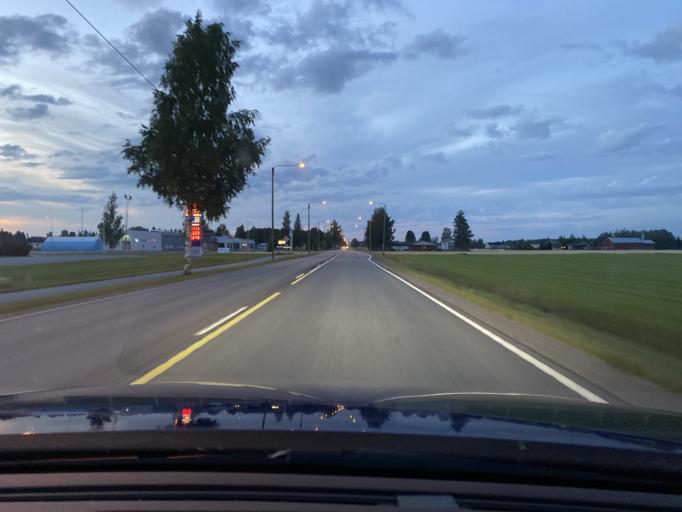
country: FI
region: Southern Ostrobothnia
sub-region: Suupohja
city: Kauhajoki
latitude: 62.4290
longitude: 22.2033
